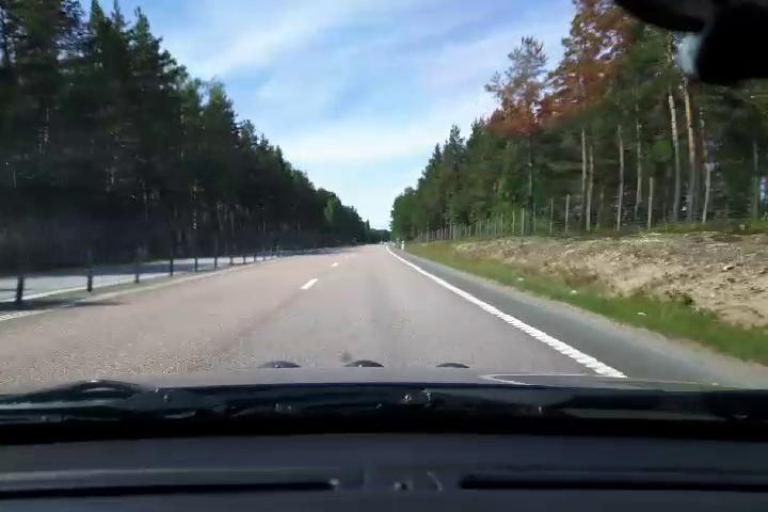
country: SE
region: Gaevleborg
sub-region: Gavle Kommun
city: Norrsundet
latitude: 60.9974
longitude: 16.9946
